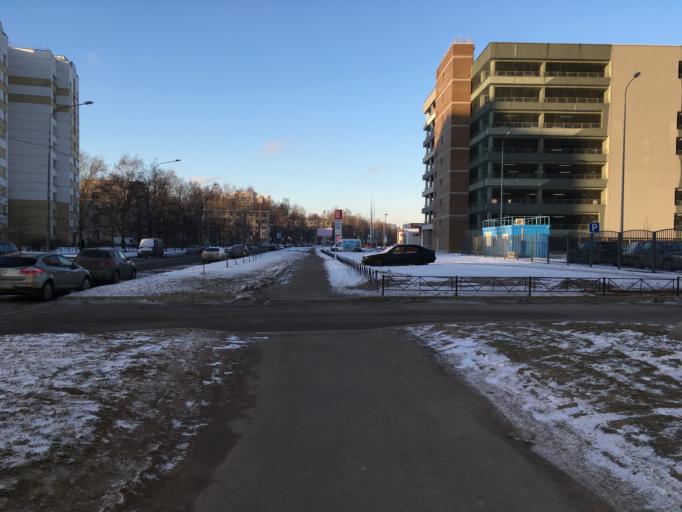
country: RU
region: St.-Petersburg
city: Krasnogvargeisky
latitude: 59.9769
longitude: 30.4358
